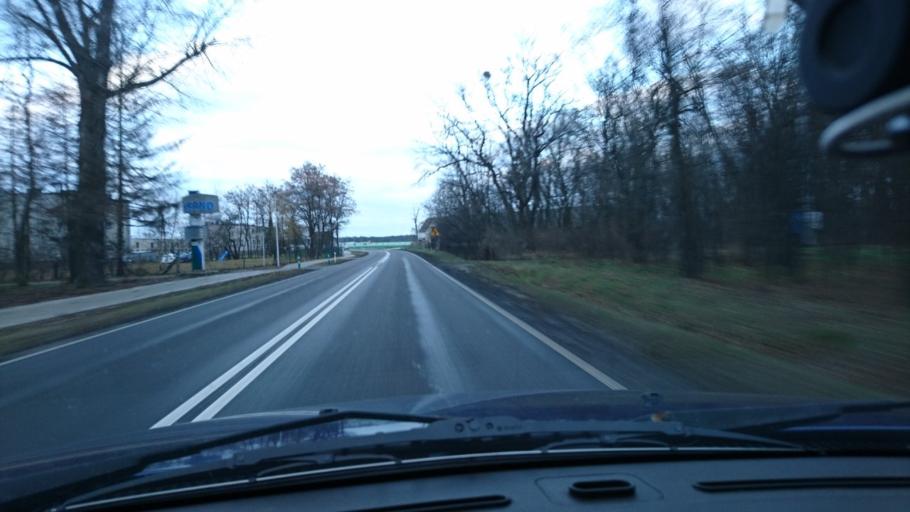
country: PL
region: Greater Poland Voivodeship
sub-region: Powiat kepinski
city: Kepno
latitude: 51.3135
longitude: 17.9836
